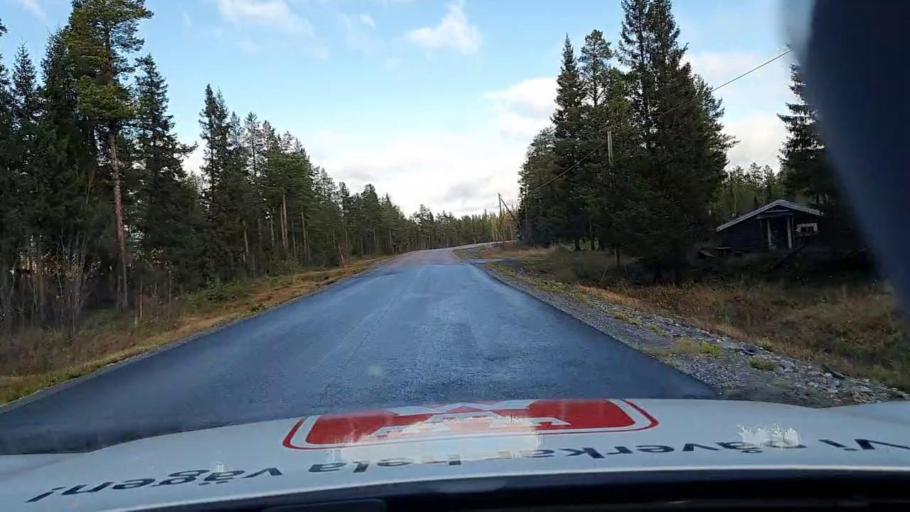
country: SE
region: Jaemtland
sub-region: Krokoms Kommun
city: Valla
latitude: 63.1585
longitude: 13.9748
